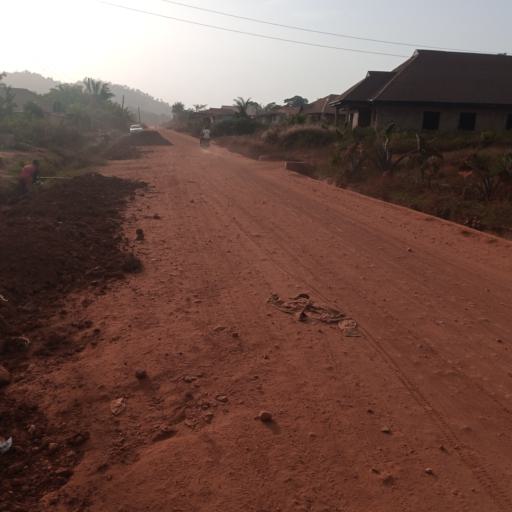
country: NG
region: Osun
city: Ilesa
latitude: 7.6215
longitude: 4.7041
